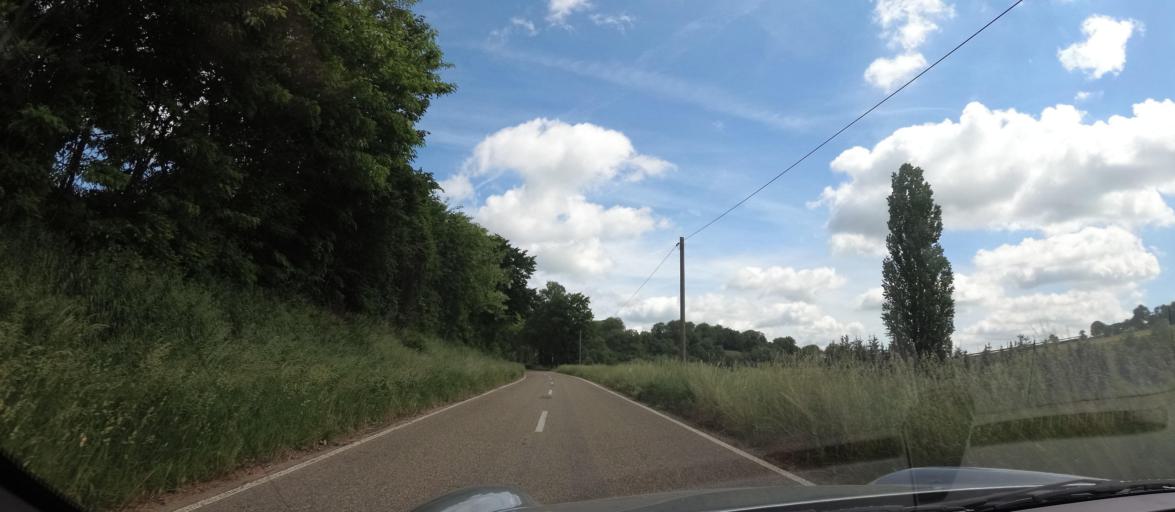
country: DE
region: Baden-Wuerttemberg
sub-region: Karlsruhe Region
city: Zaisenhausen
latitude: 49.1522
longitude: 8.8114
